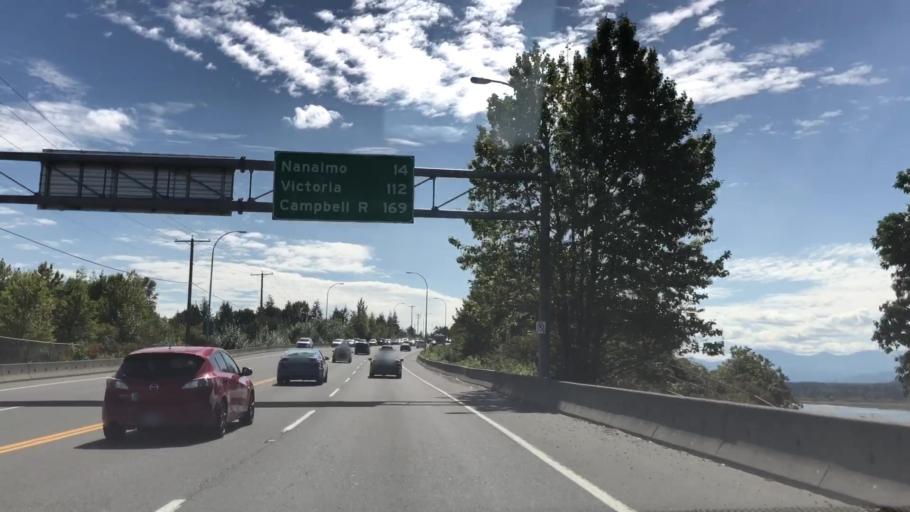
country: CA
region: British Columbia
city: Nanaimo
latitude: 49.1497
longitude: -123.8880
